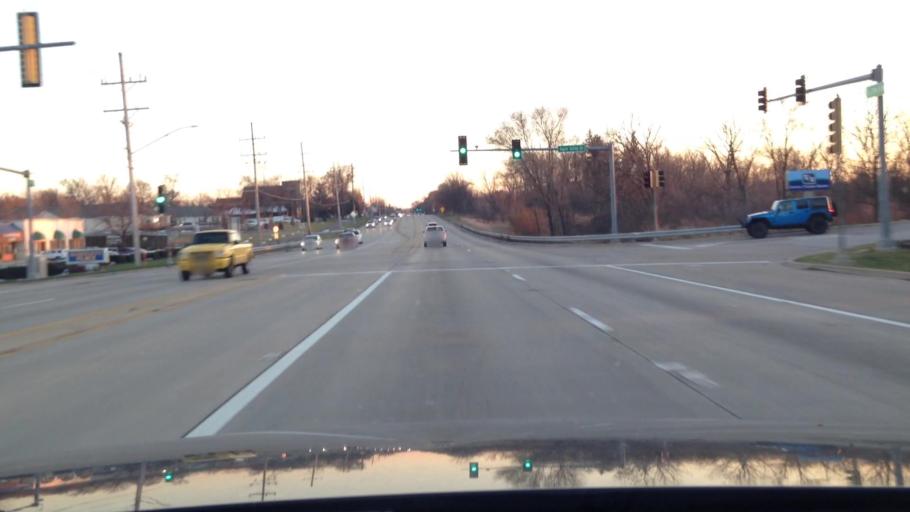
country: US
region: Illinois
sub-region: Cook County
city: Bartlett
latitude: 41.9723
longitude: -88.2071
